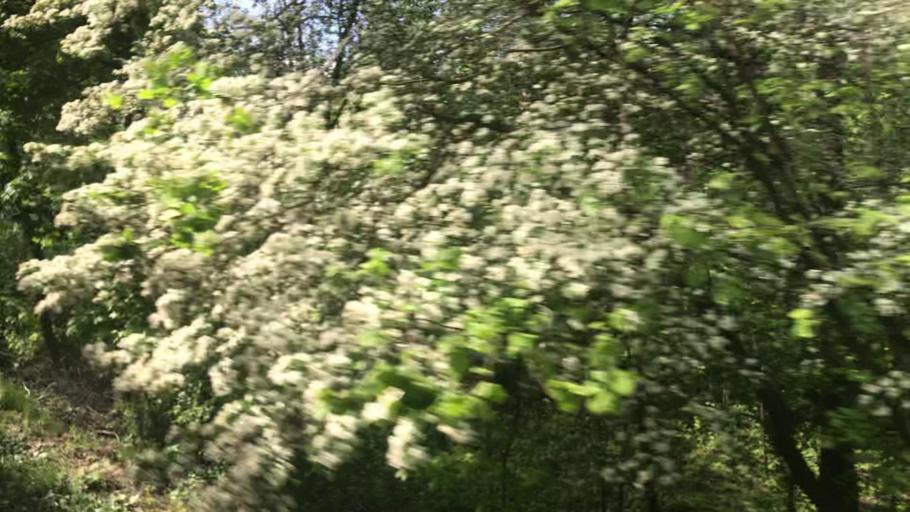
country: PL
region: Lower Silesian Voivodeship
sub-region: Powiat swidnicki
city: Swiebodzice
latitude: 50.8303
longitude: 16.3281
